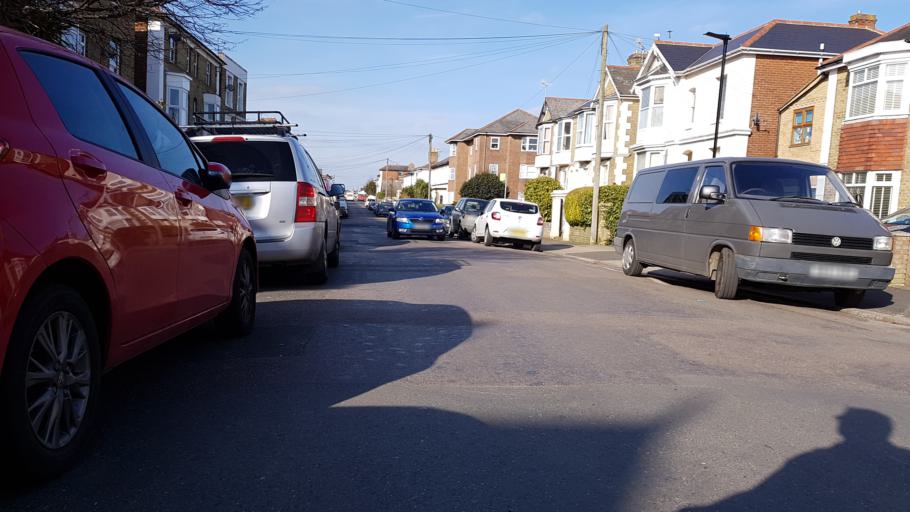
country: GB
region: England
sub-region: Isle of Wight
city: Ryde
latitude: 50.7259
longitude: -1.1559
